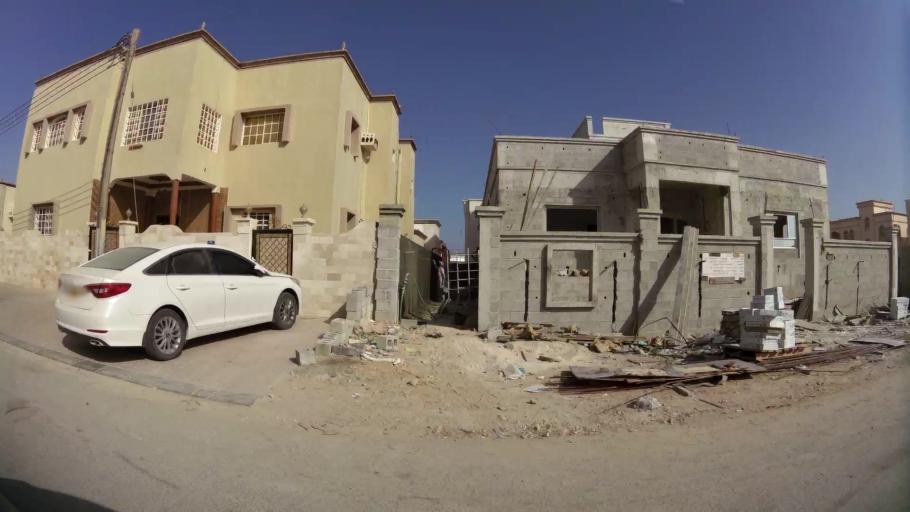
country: OM
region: Zufar
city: Salalah
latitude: 17.0080
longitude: 54.0179
